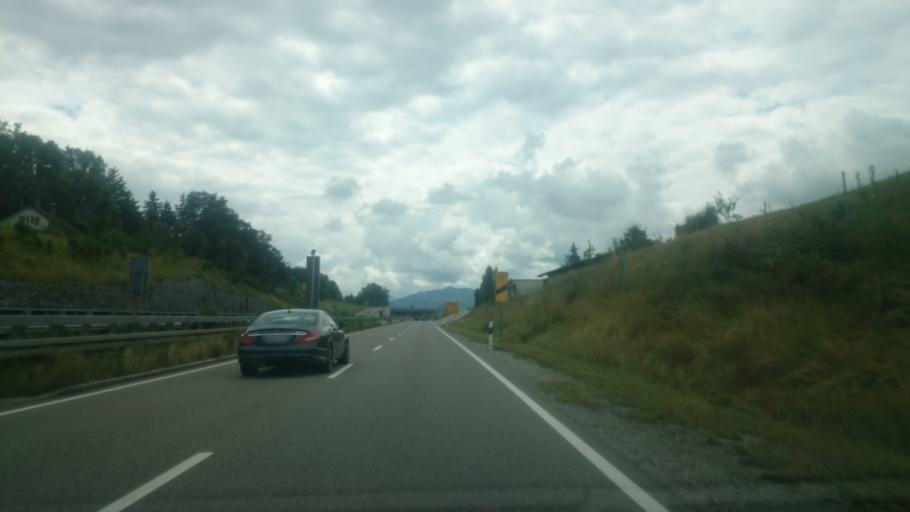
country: DE
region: Bavaria
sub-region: Swabia
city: Waltenhofen
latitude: 47.6330
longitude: 10.2818
